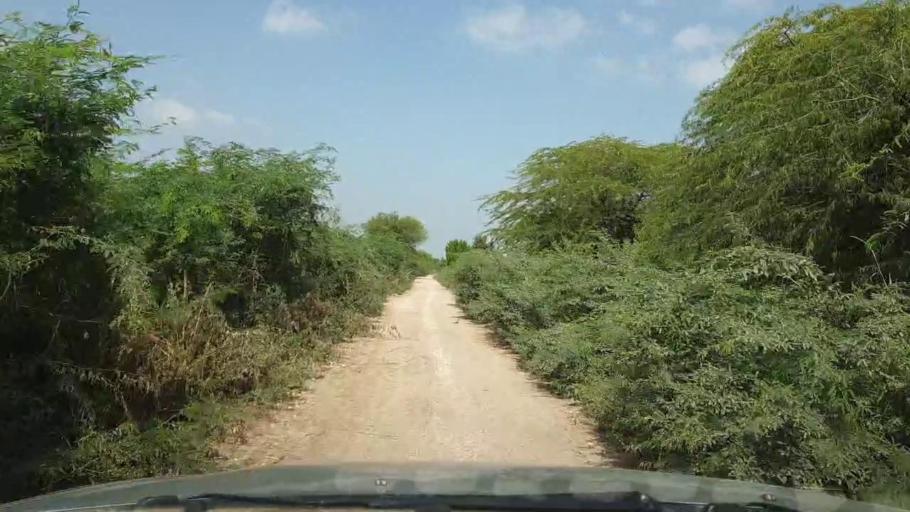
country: PK
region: Sindh
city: Rajo Khanani
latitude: 25.0270
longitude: 68.9165
